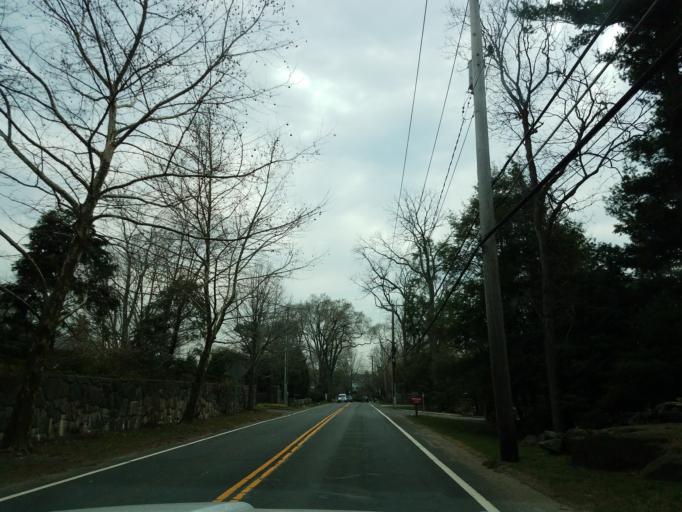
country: US
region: Connecticut
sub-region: Fairfield County
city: Greenwich
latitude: 41.0390
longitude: -73.6343
